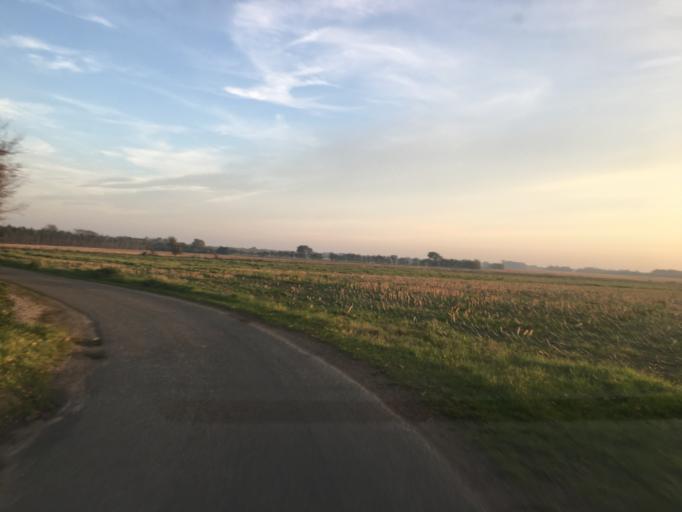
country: DK
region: South Denmark
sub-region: Tonder Kommune
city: Toftlund
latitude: 55.0332
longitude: 9.1169
